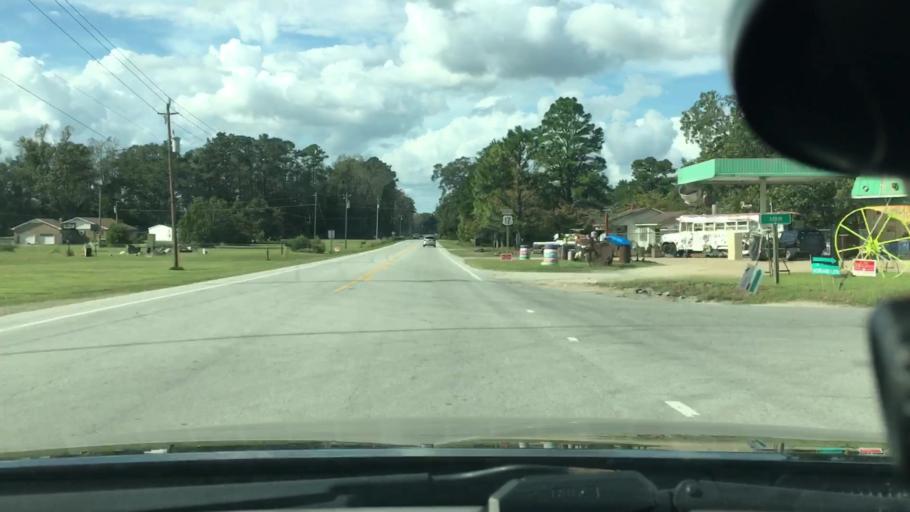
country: US
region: North Carolina
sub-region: Craven County
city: New Bern
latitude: 35.2206
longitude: -77.0664
